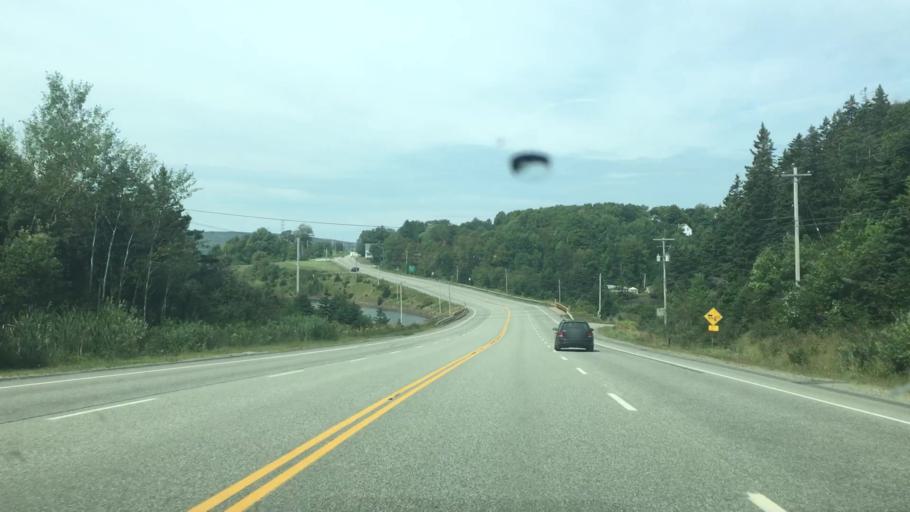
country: CA
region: Nova Scotia
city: Port Hawkesbury
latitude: 45.6434
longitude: -61.3954
